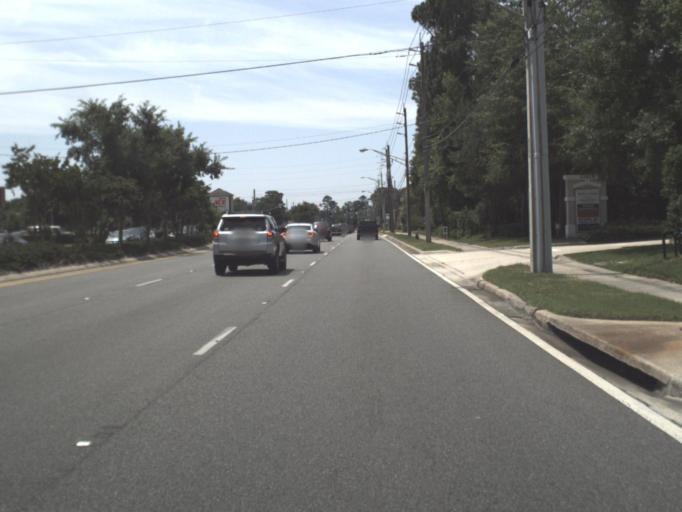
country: US
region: Florida
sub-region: Saint Johns County
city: Fruit Cove
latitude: 30.1426
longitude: -81.6327
